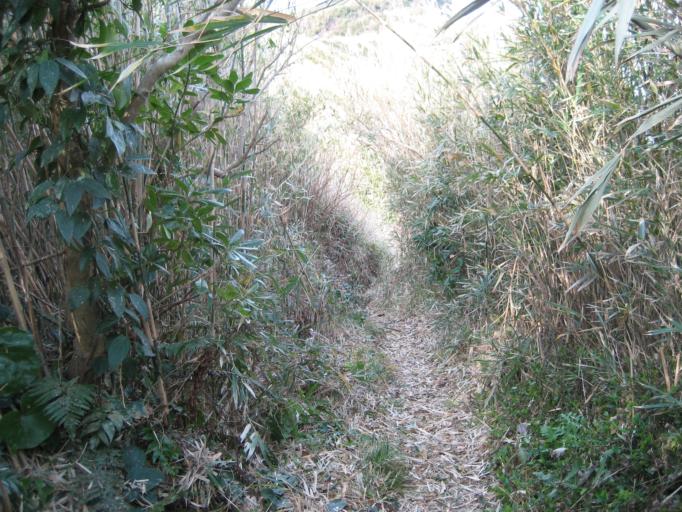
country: JP
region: Shizuoka
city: Ito
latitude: 34.7963
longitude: 139.3663
